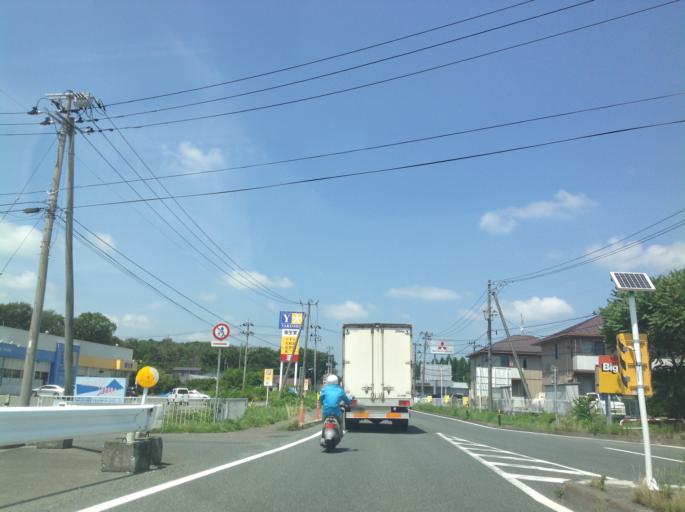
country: JP
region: Iwate
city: Hanamaki
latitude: 39.3380
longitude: 141.1085
